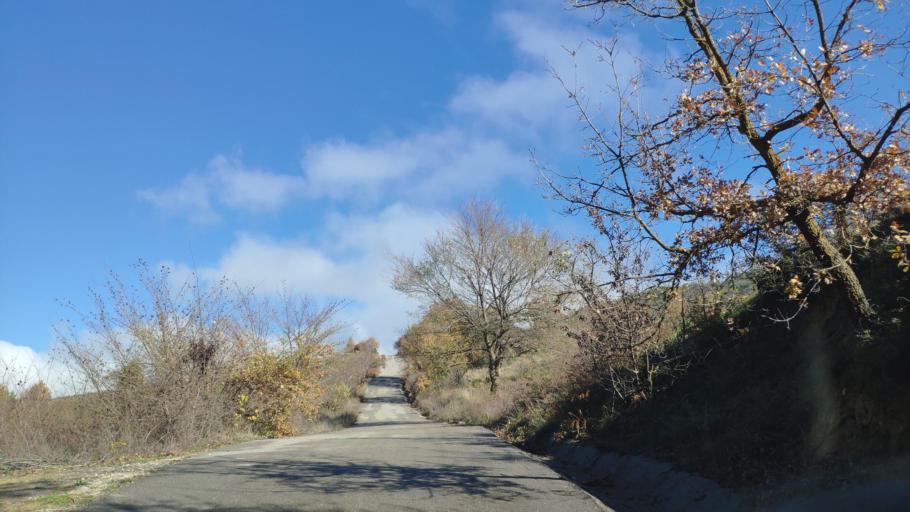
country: GR
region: West Greece
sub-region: Nomos Achaias
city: Aiyira
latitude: 38.0656
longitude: 22.4644
